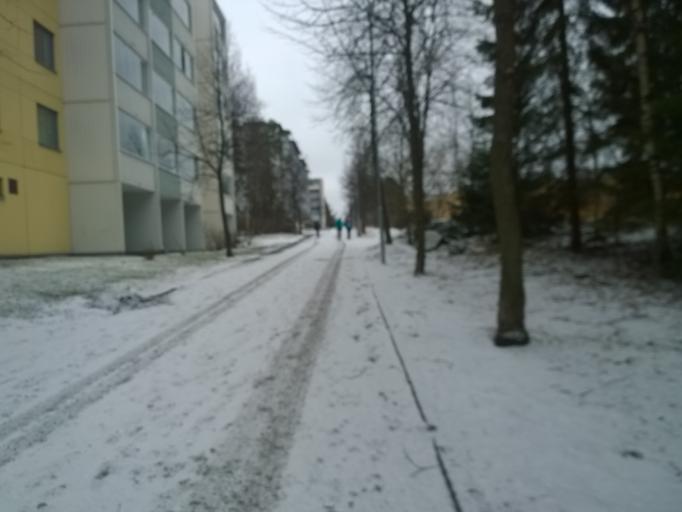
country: FI
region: Pirkanmaa
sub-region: Tampere
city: Tampere
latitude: 61.4432
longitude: 23.8473
